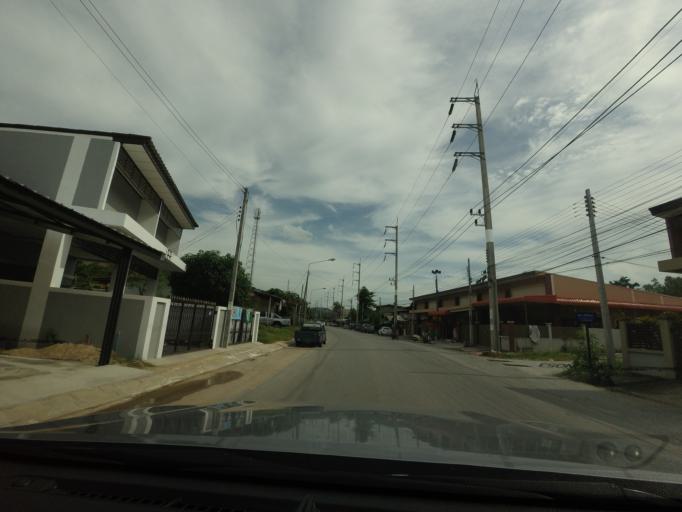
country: TH
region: Yala
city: Yala
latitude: 6.5271
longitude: 101.2904
